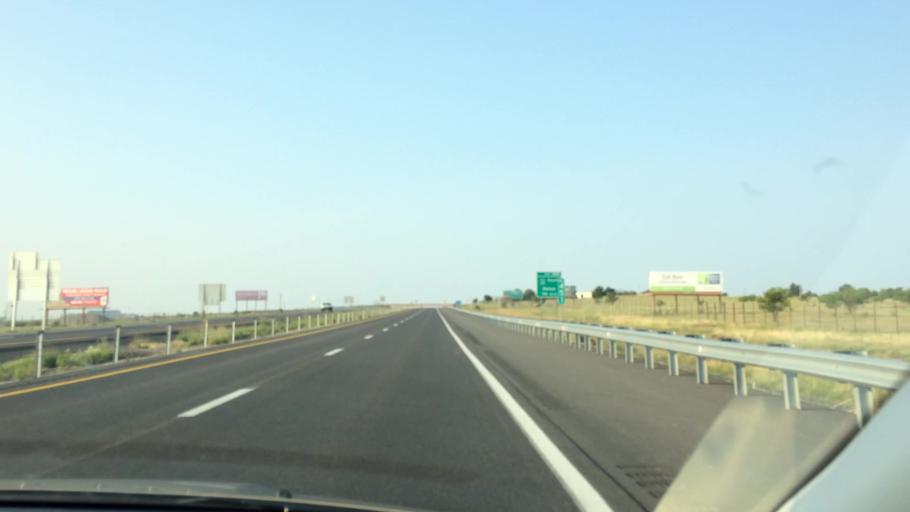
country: US
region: New Mexico
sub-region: Colfax County
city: Raton
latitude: 36.8774
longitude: -104.4343
